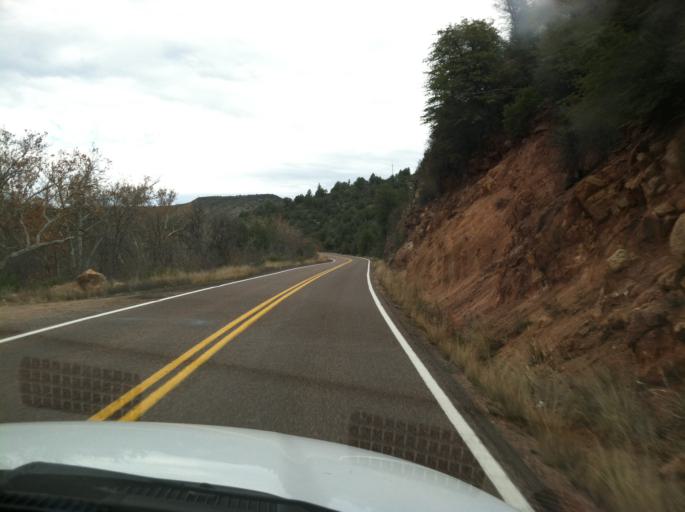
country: US
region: Arizona
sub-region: Gila County
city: Payson
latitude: 34.3030
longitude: -111.3589
